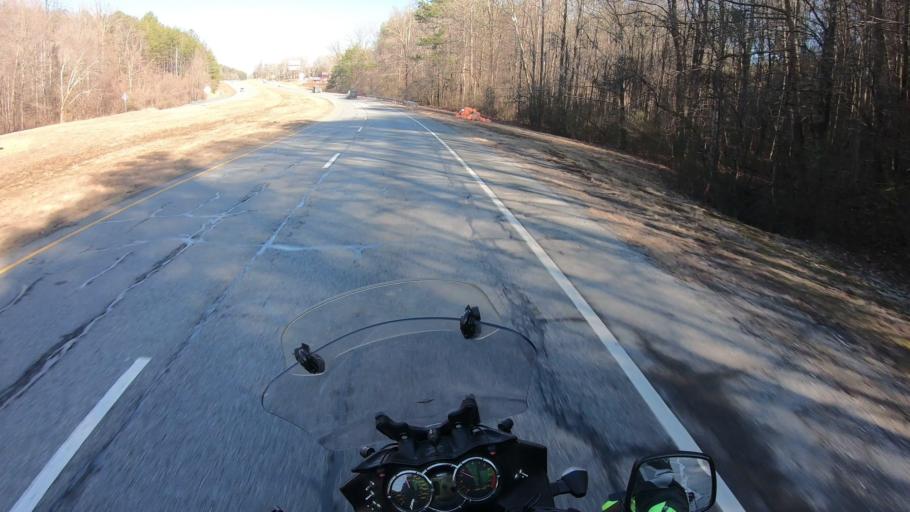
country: US
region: Georgia
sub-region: Gilmer County
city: Ellijay
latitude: 34.7271
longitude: -84.4377
